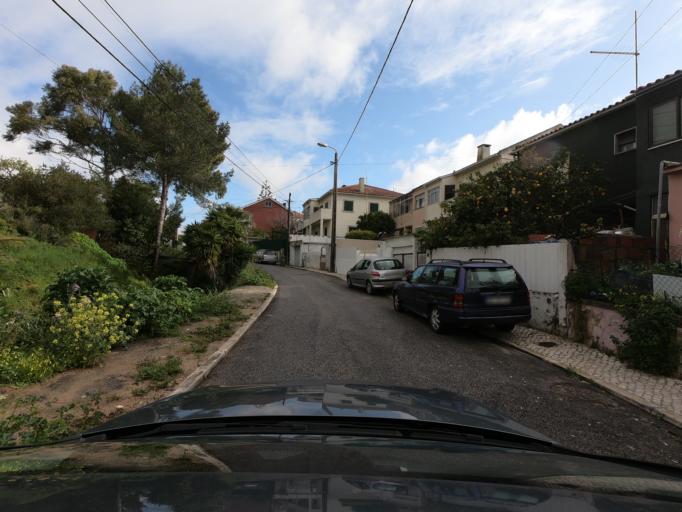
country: PT
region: Lisbon
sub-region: Oeiras
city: Porto Salvo
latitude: 38.7217
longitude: -9.3102
